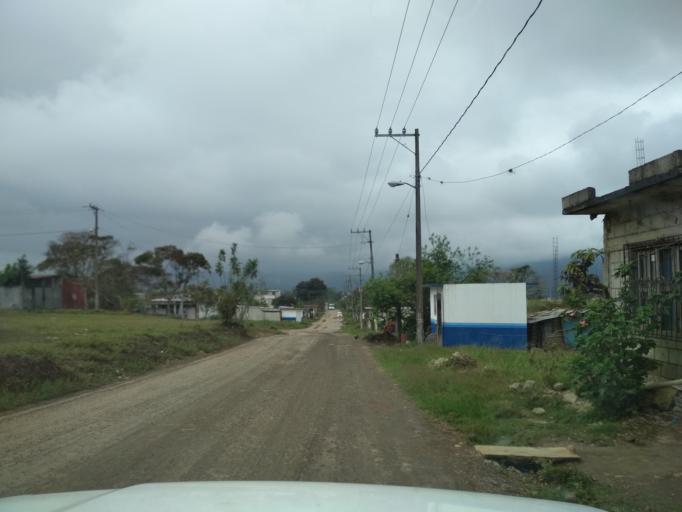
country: MX
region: Veracruz
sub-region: Cordoba
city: San Jose de Tapia
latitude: 18.8465
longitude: -96.9677
